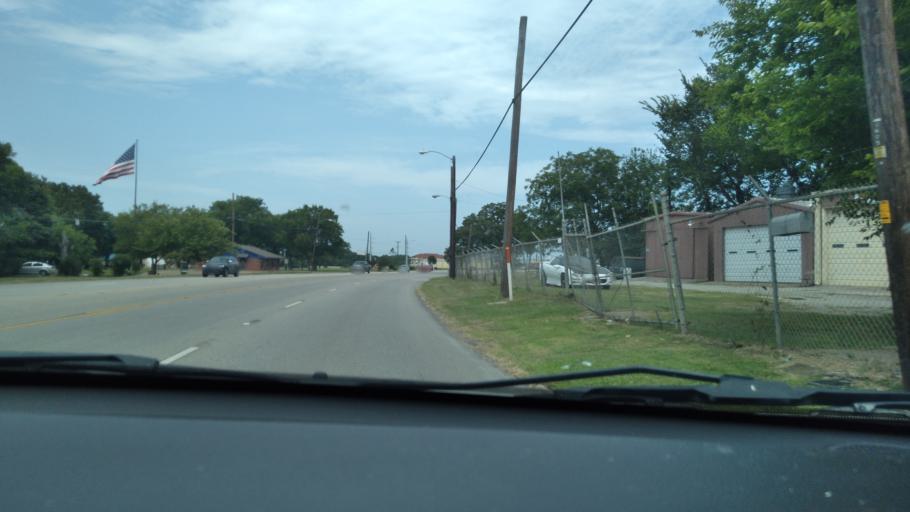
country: US
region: Texas
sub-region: Navarro County
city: Corsicana
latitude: 32.0987
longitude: -96.4487
